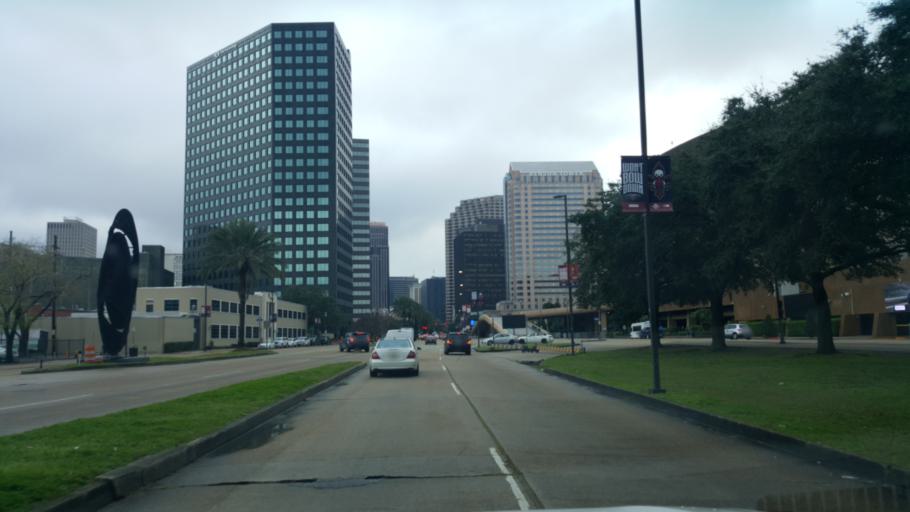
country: US
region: Louisiana
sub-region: Orleans Parish
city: New Orleans
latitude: 29.9532
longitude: -90.0823
